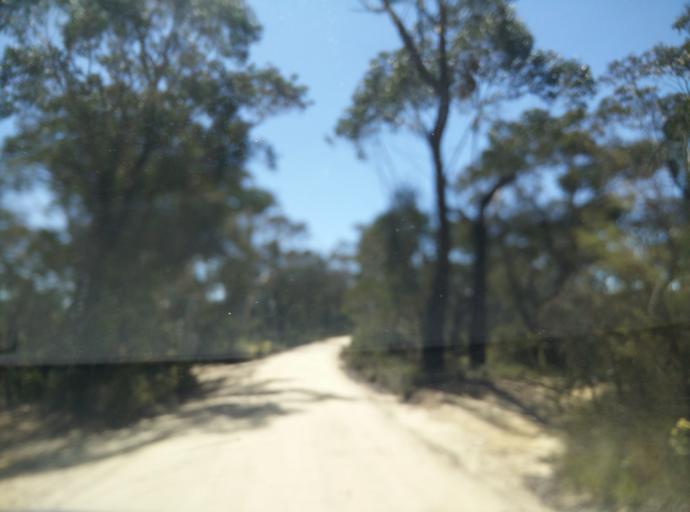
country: AU
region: New South Wales
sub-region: Blue Mountains Municipality
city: Blackheath
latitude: -33.5686
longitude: 150.2803
